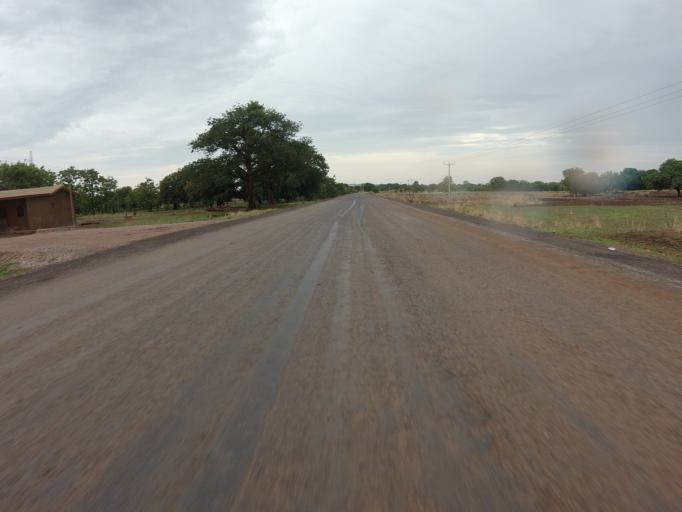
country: GH
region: Upper East
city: Bolgatanga
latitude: 10.8627
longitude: -0.6610
